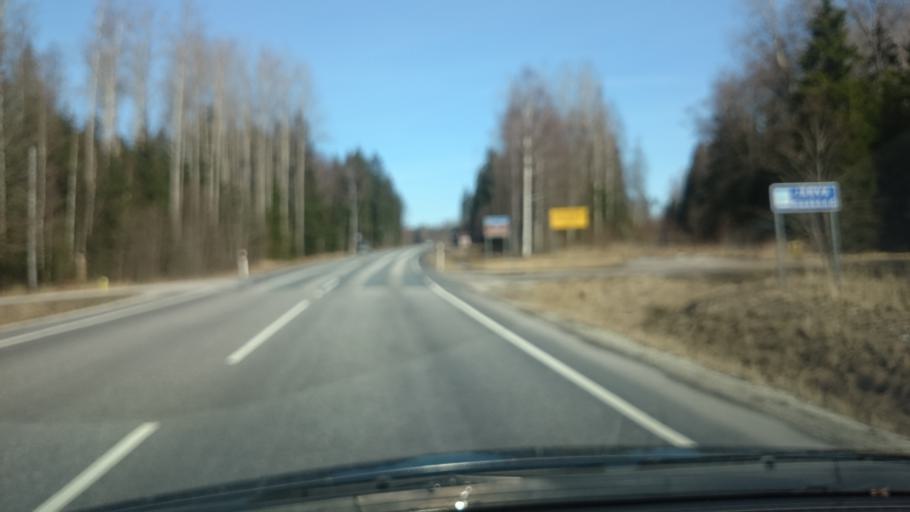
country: EE
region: Jaervamaa
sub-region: Tueri vald
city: Sarevere
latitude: 58.7168
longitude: 25.2738
